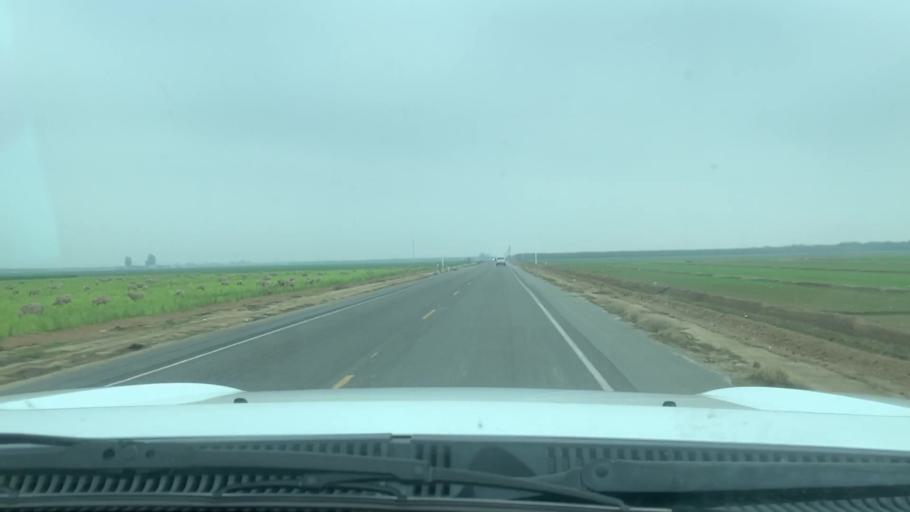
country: US
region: California
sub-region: Kern County
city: Wasco
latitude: 35.5002
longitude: -119.3833
